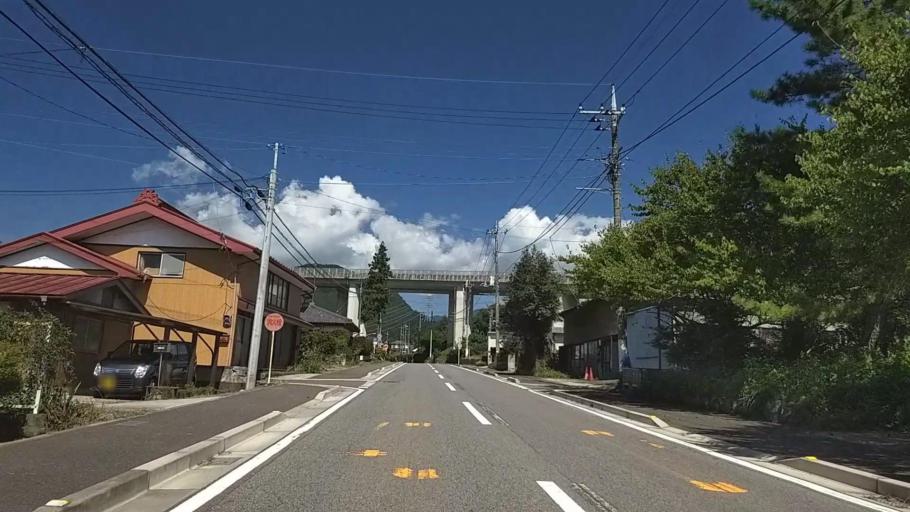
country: JP
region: Gunma
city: Annaka
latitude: 36.3432
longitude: 138.7243
